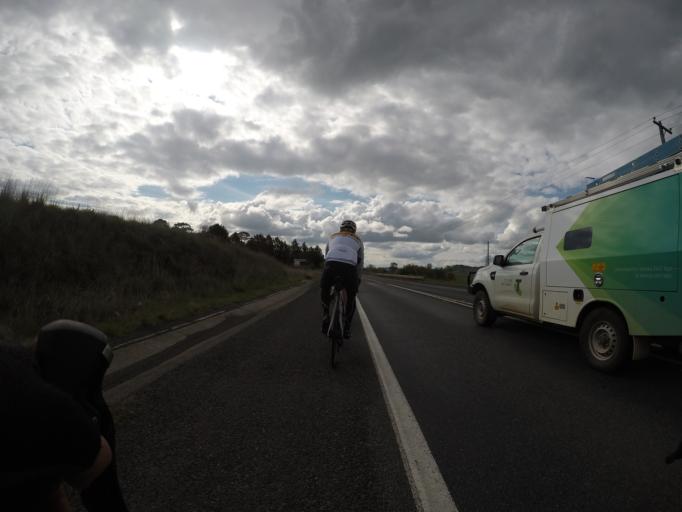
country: AU
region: New South Wales
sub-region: Blayney
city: Millthorpe
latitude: -33.3529
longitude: 149.1697
